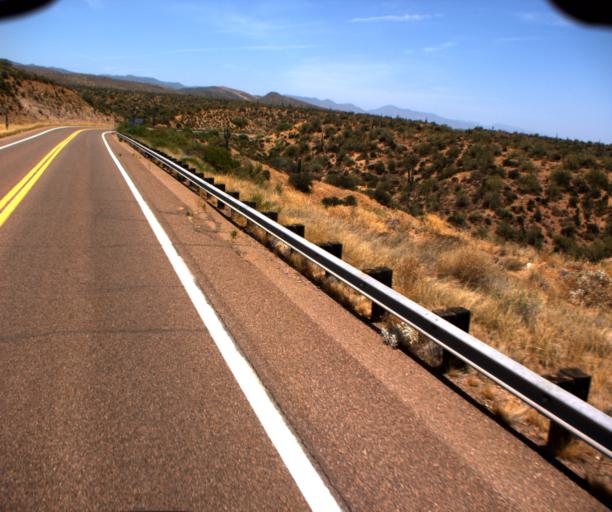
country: US
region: Arizona
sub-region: Gila County
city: Tonto Basin
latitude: 33.6987
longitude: -111.1860
